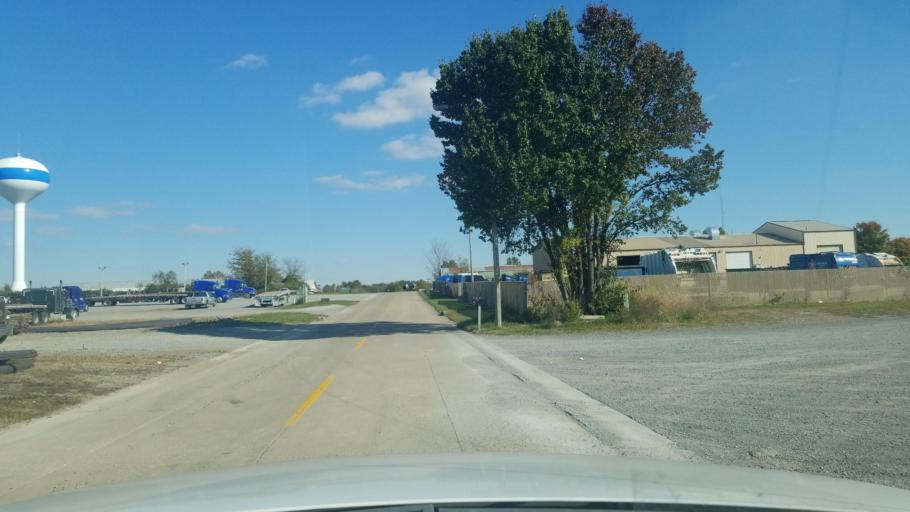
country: US
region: Illinois
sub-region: Williamson County
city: Energy
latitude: 37.7397
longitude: -88.9866
